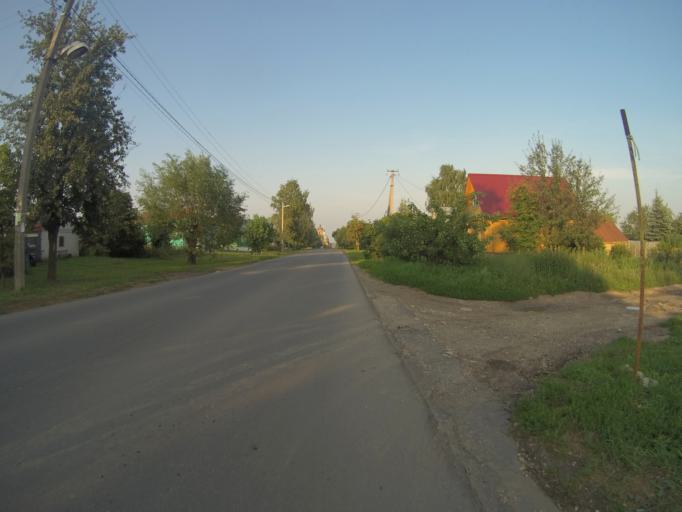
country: RU
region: Vladimir
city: Bogolyubovo
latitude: 56.2973
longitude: 40.5622
